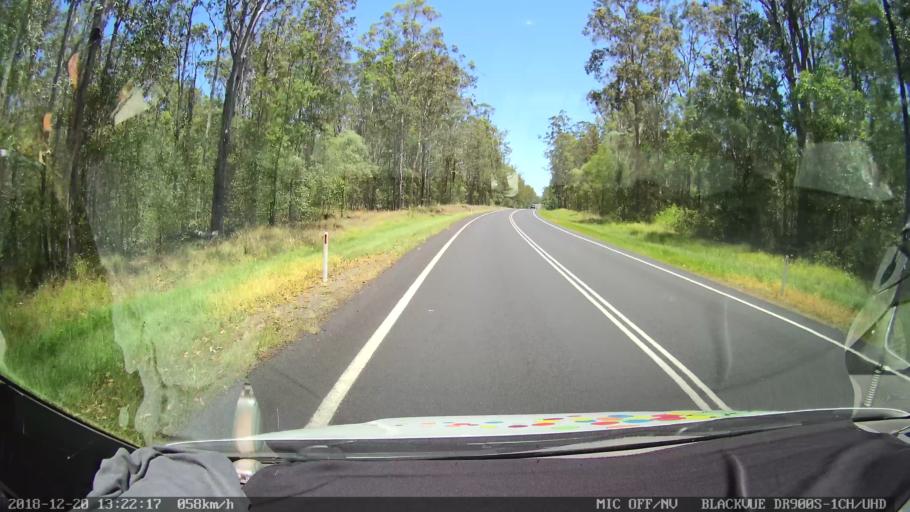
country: AU
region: New South Wales
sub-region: Richmond Valley
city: Casino
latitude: -29.0903
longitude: 153.0015
